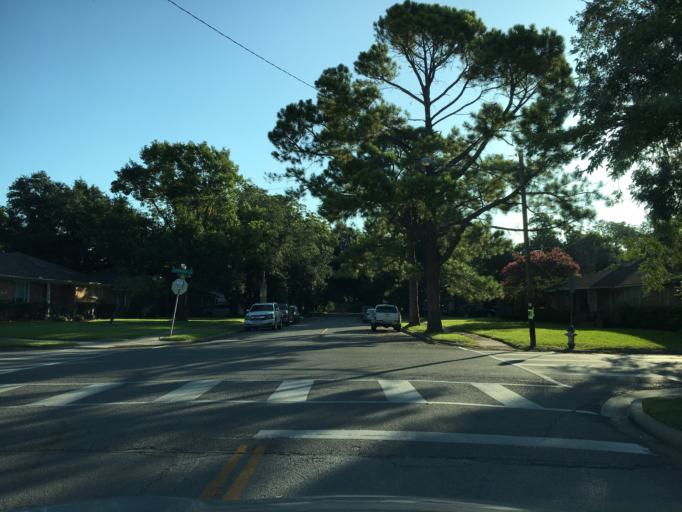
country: US
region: Texas
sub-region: Dallas County
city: Highland Park
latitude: 32.8587
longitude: -96.7388
